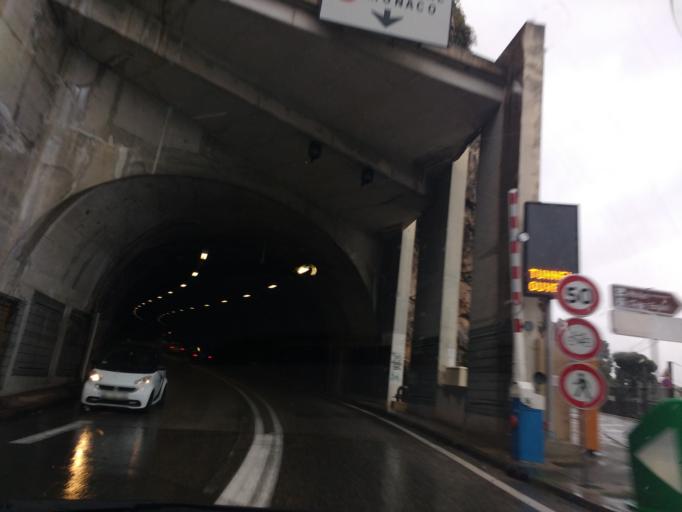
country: FR
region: Provence-Alpes-Cote d'Azur
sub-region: Departement des Alpes-Maritimes
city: Eze
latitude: 43.7205
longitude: 7.3687
